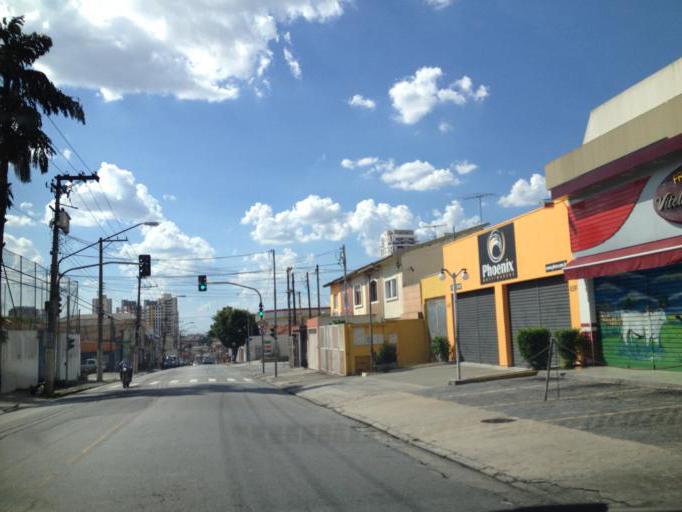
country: BR
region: Sao Paulo
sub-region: Sao Paulo
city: Sao Paulo
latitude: -23.5623
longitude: -46.5736
